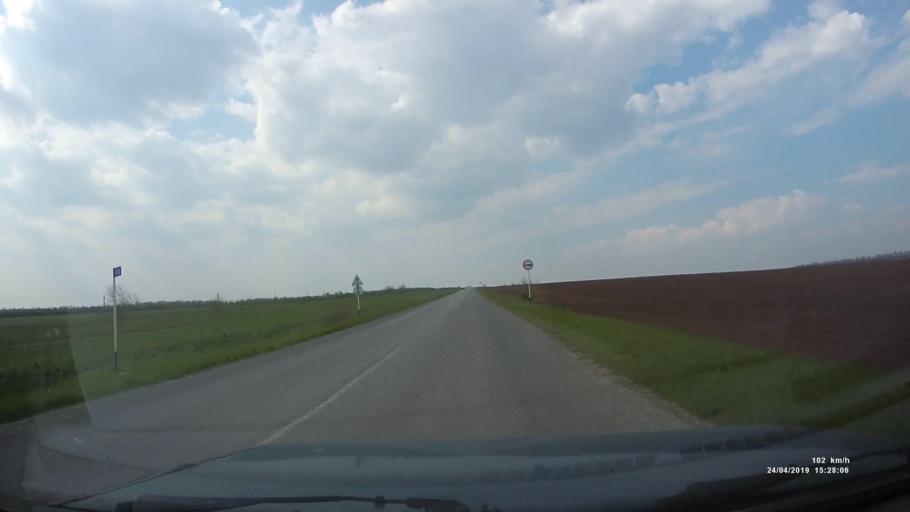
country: RU
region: Rostov
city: Remontnoye
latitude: 46.5743
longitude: 43.0207
